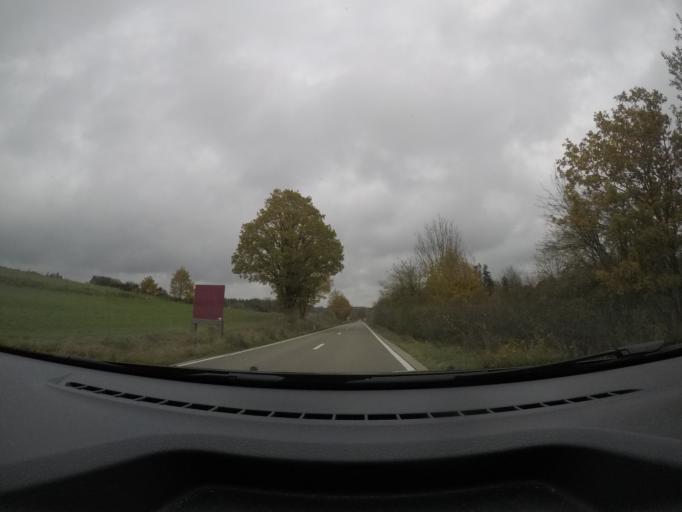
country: BE
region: Wallonia
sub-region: Province du Luxembourg
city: Bertogne
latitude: 50.0915
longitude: 5.7249
